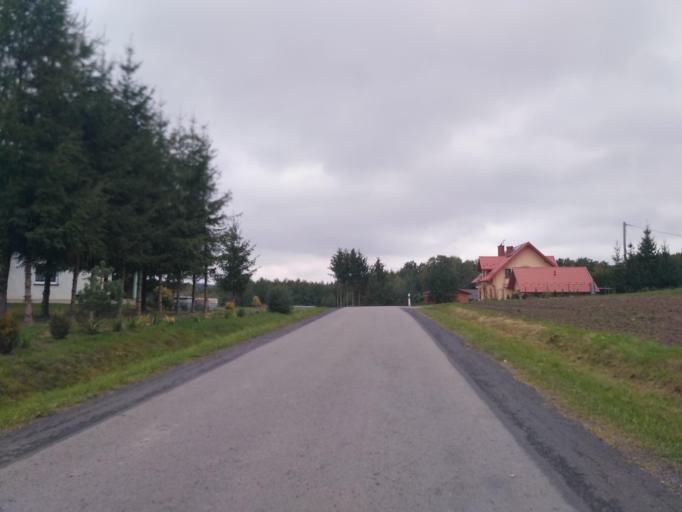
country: PL
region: Subcarpathian Voivodeship
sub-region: Powiat debicki
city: Brzostek
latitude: 49.9199
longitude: 21.4666
